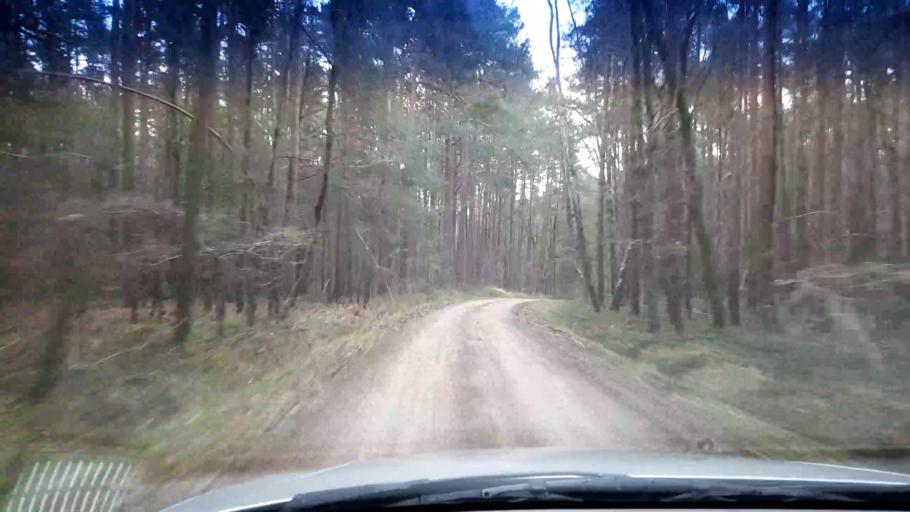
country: DE
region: Bavaria
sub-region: Upper Franconia
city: Lauter
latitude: 49.9455
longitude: 10.7825
